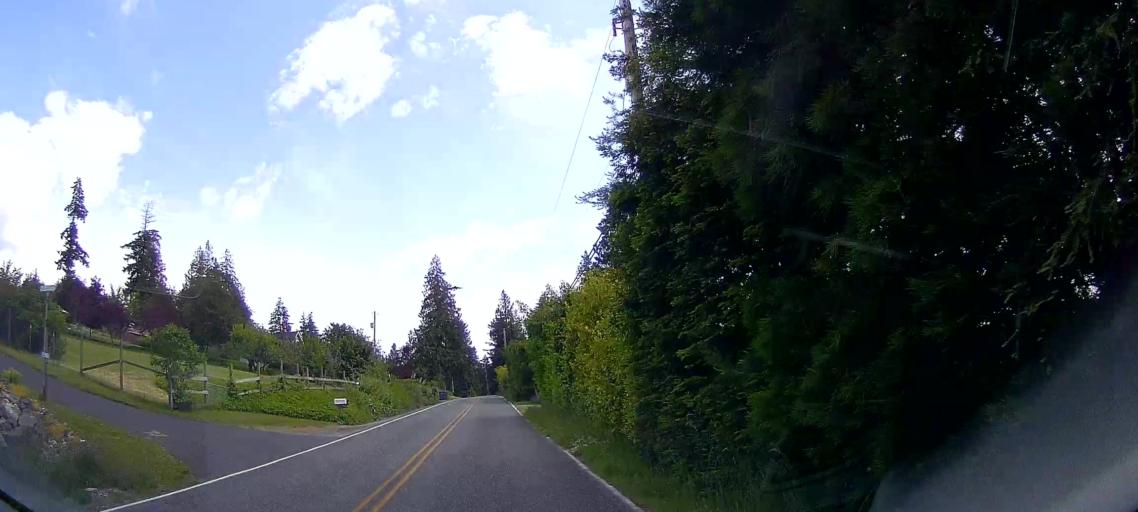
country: US
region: Washington
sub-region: Skagit County
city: Burlington
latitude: 48.5765
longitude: -122.3997
